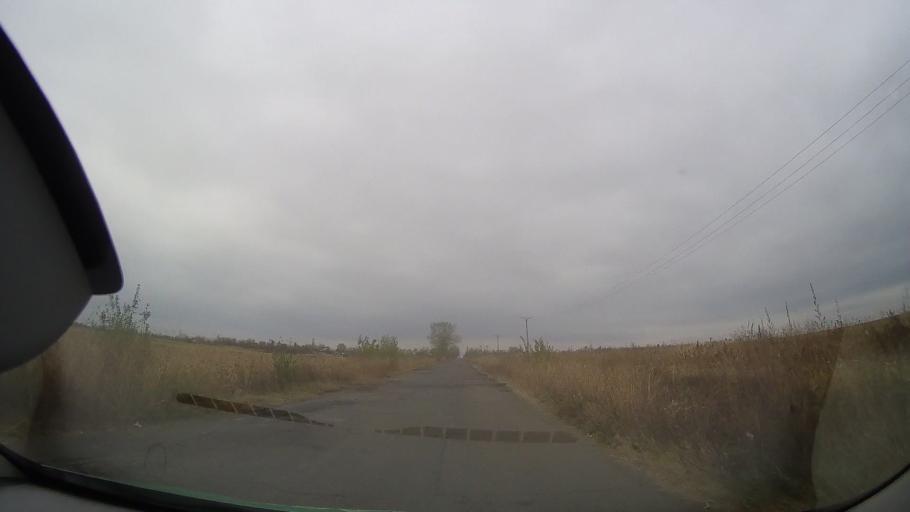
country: RO
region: Braila
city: Dudesti
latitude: 44.9373
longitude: 27.4255
